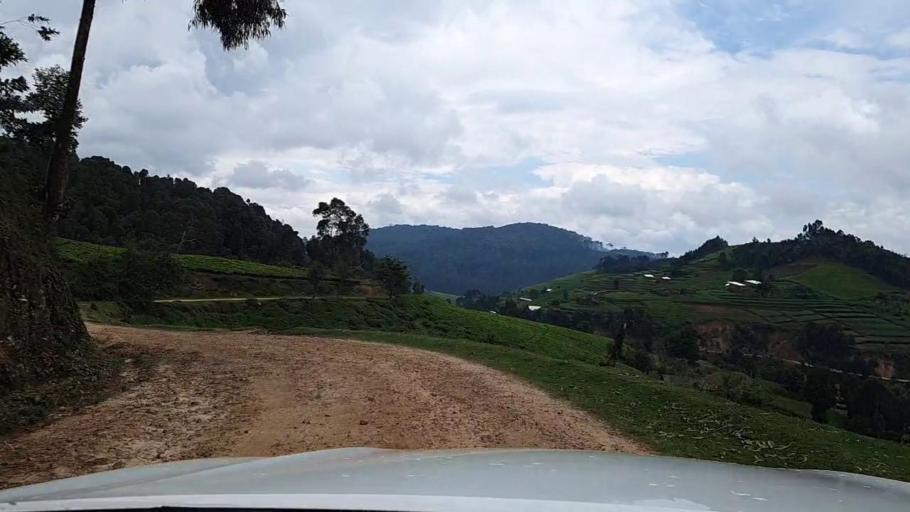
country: RW
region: Western Province
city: Kibuye
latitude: -2.2894
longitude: 29.3716
